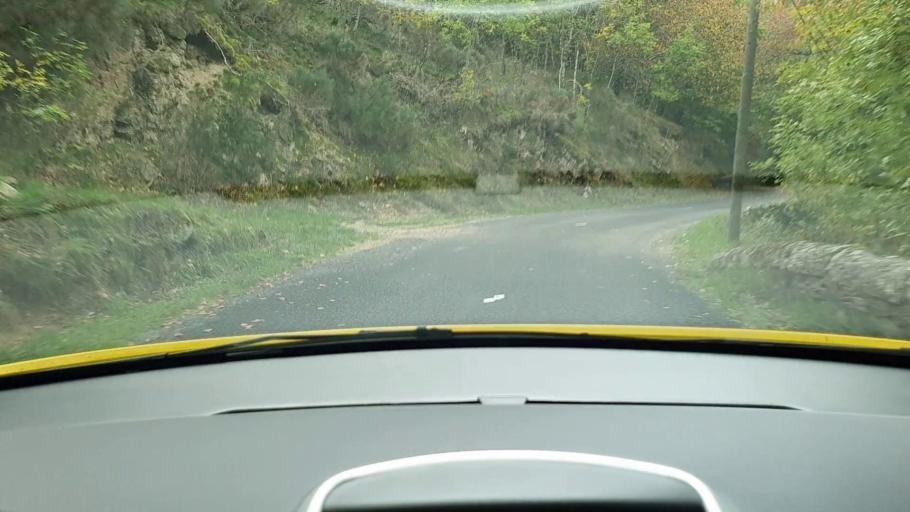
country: FR
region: Languedoc-Roussillon
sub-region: Departement de la Lozere
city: Meyrueis
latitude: 44.0616
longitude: 3.4407
